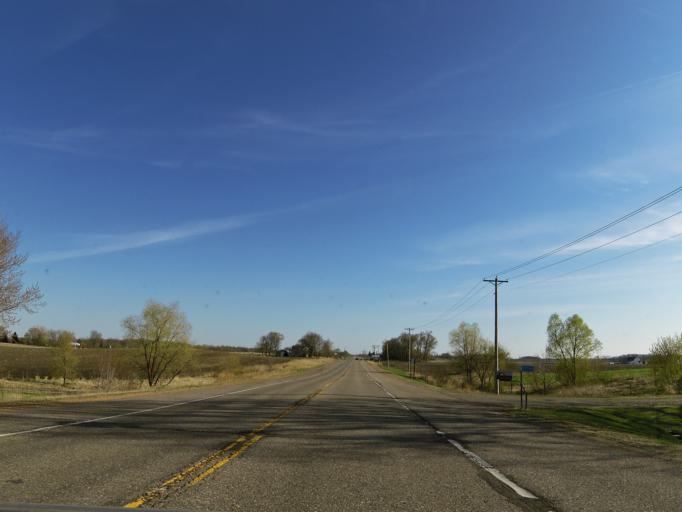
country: US
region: Minnesota
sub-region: Scott County
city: Prior Lake
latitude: 44.6929
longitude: -93.5010
